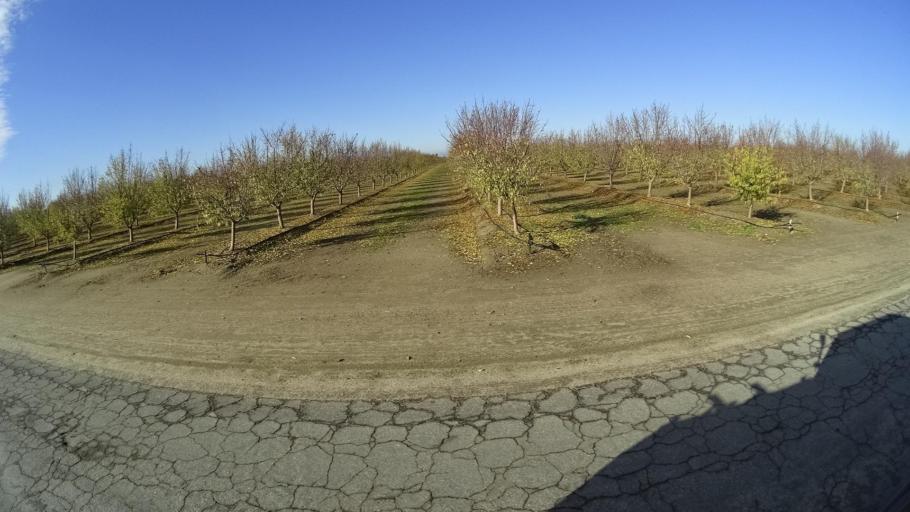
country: US
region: California
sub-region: Kern County
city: Delano
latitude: 35.7217
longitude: -119.3030
